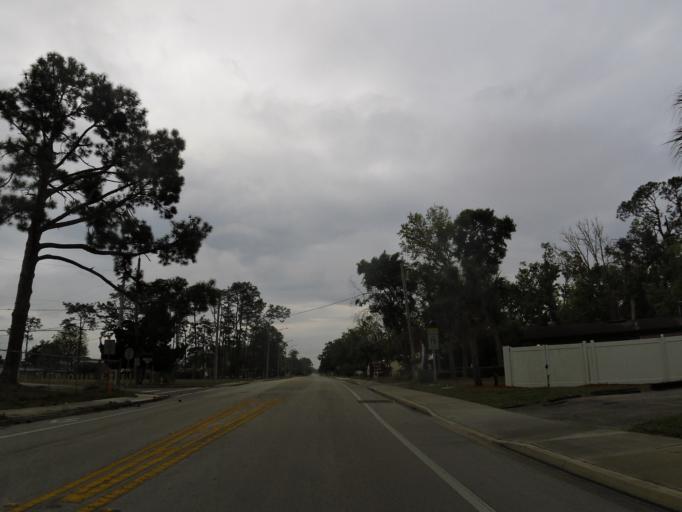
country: US
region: Florida
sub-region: Duval County
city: Jacksonville
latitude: 30.2797
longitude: -81.6179
